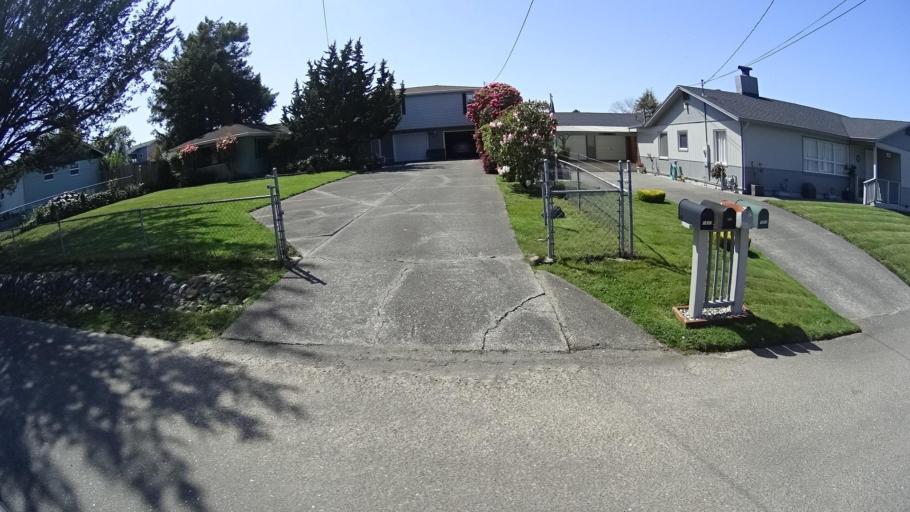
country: US
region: California
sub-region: Humboldt County
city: Hydesville
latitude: 40.5642
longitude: -124.1340
